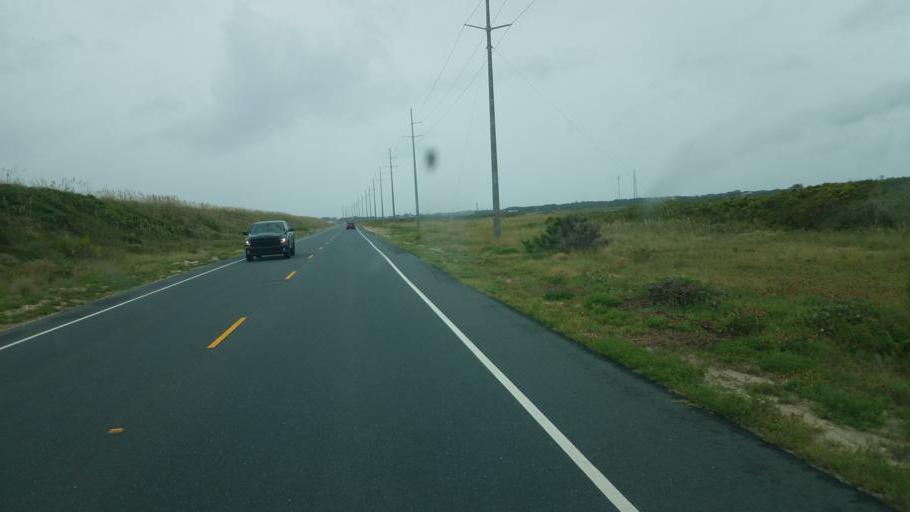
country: US
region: North Carolina
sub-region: Dare County
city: Buxton
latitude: 35.2787
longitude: -75.5174
